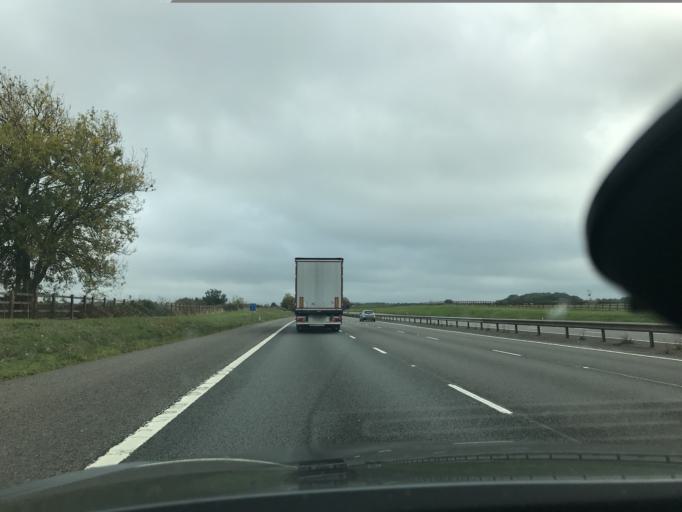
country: GB
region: England
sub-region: Warwickshire
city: Warwick
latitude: 52.2503
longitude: -1.5713
